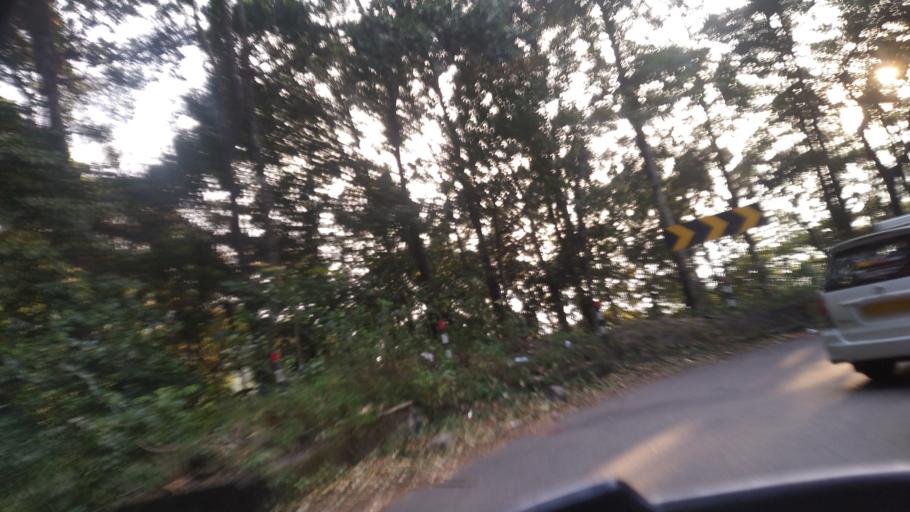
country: IN
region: Kerala
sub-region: Wayanad
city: Kalpetta
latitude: 11.5037
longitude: 76.0273
